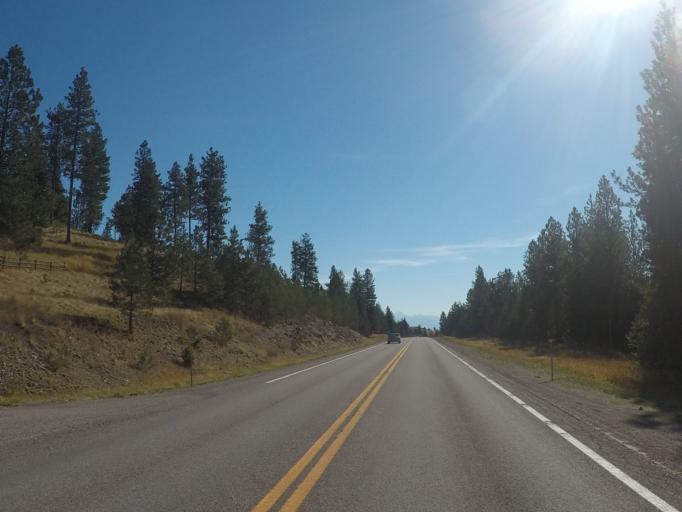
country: US
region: Montana
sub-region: Lake County
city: Polson
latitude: 47.7639
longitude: -114.2374
